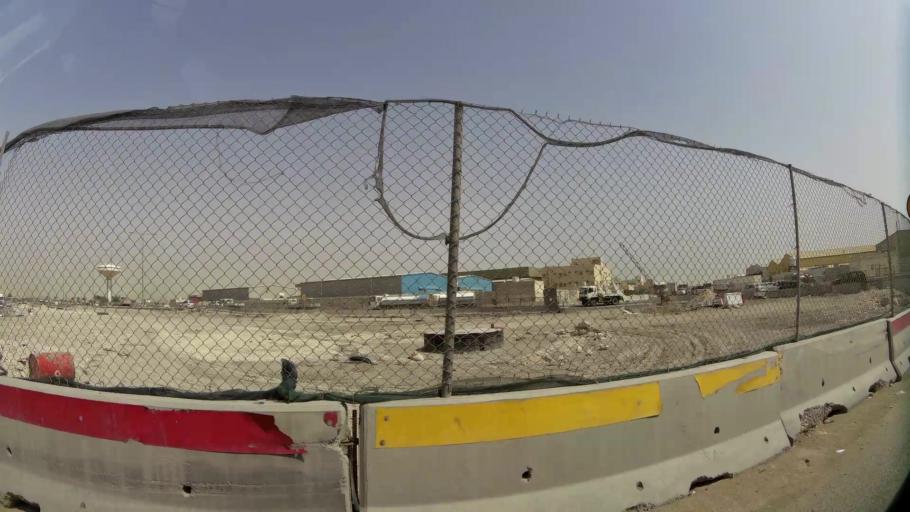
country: QA
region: Baladiyat ar Rayyan
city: Ar Rayyan
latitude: 25.2044
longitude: 51.4105
